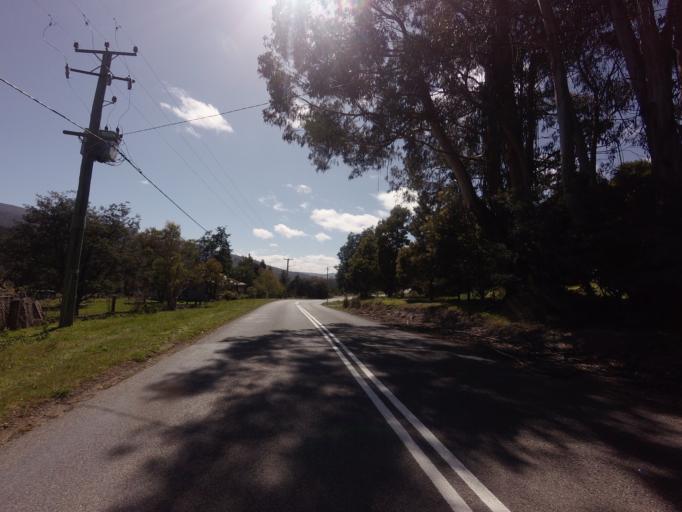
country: AU
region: Tasmania
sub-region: Derwent Valley
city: New Norfolk
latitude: -42.7477
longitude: 146.6491
